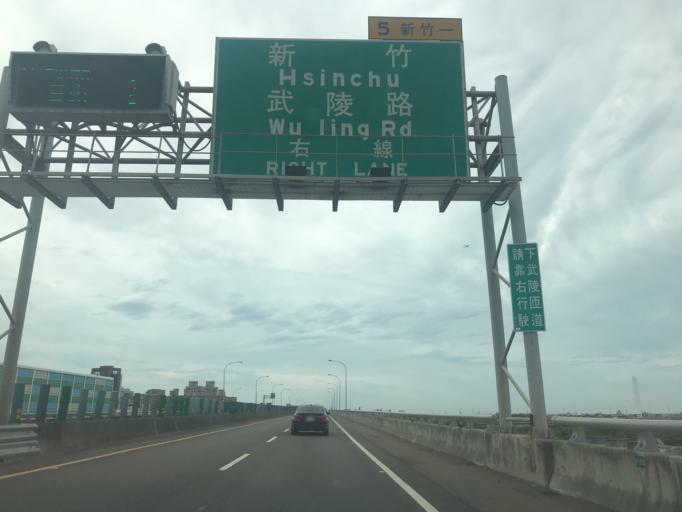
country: TW
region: Taiwan
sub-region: Hsinchu
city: Hsinchu
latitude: 24.8233
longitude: 120.9828
